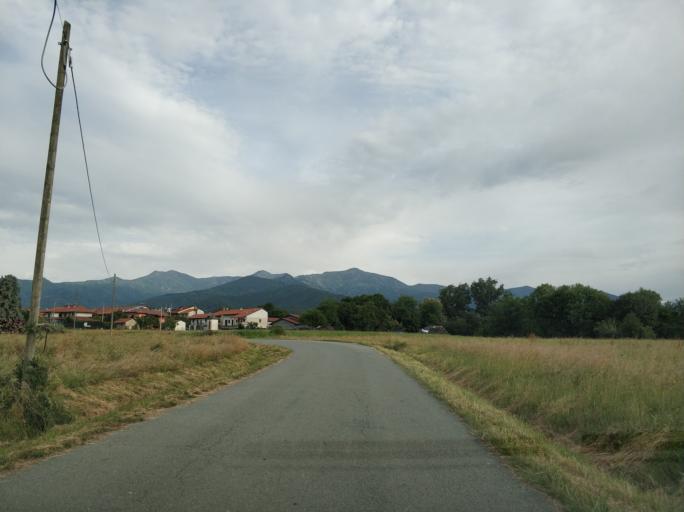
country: IT
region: Piedmont
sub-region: Provincia di Torino
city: Vauda Canavese Superiore
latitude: 45.2929
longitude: 7.6200
